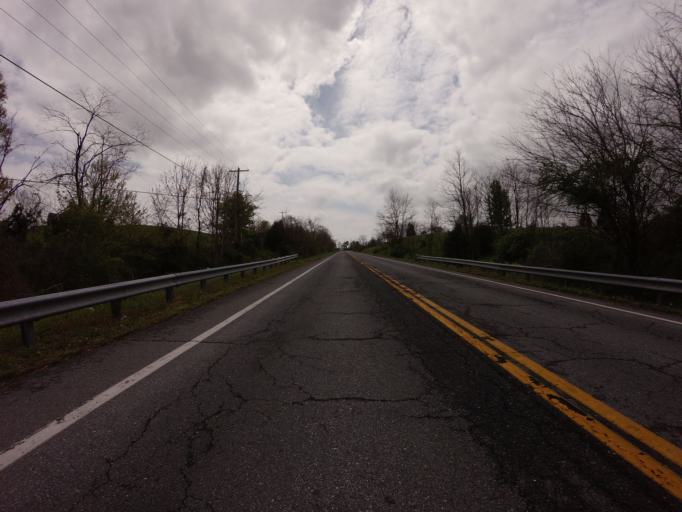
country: US
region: Maryland
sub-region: Frederick County
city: Woodsboro
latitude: 39.5512
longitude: -77.3737
